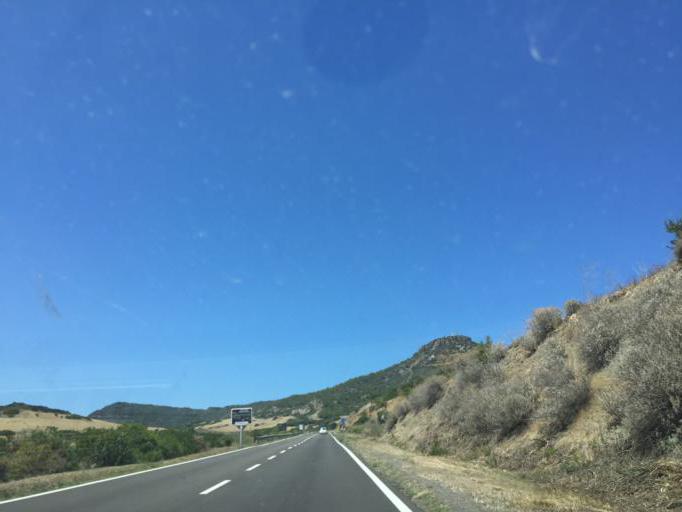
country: IT
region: Sardinia
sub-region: Provincia di Sassari
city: Valledoria
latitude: 40.9023
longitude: 8.7843
